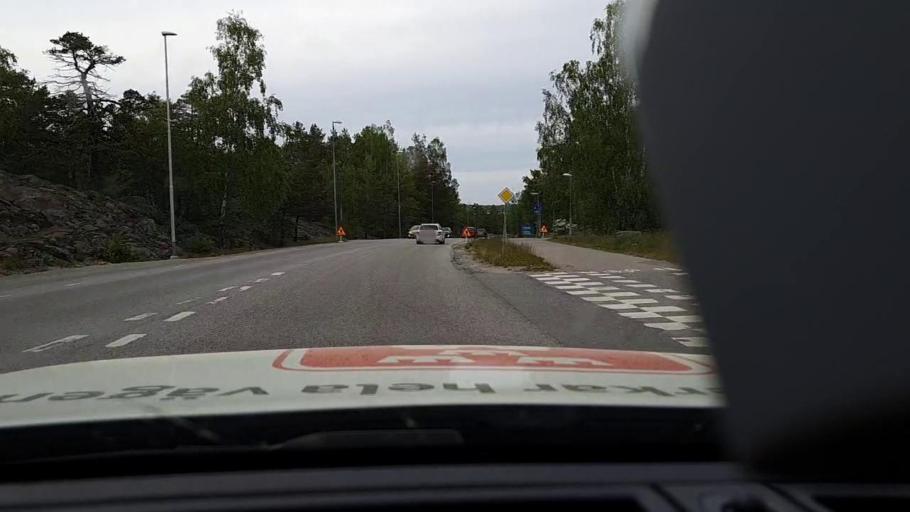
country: SE
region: Stockholm
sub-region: Haninge Kommun
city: Haninge
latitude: 59.1706
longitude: 18.1613
